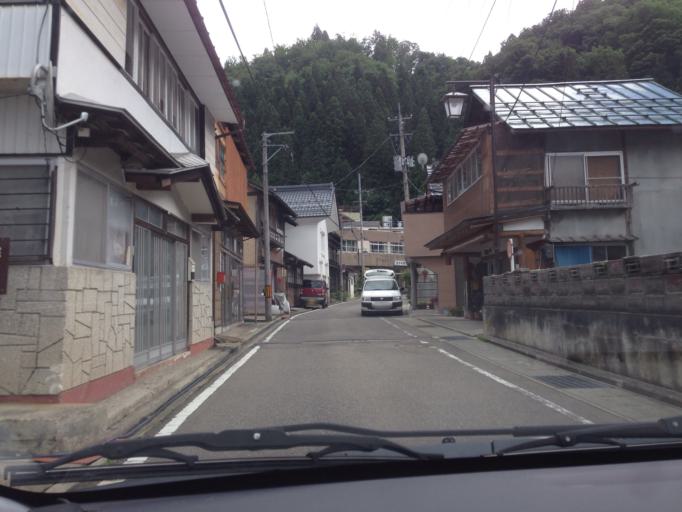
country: JP
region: Fukushima
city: Kitakata
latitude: 37.7298
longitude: 139.8869
